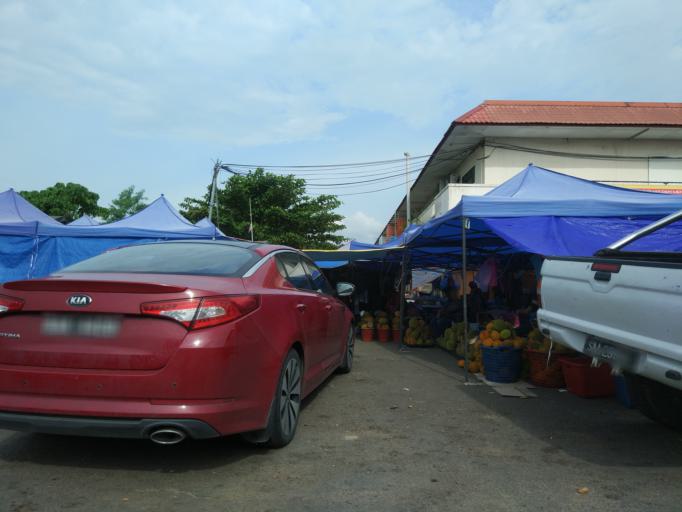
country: MY
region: Sabah
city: Beaufort
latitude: 5.0742
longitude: 115.5490
